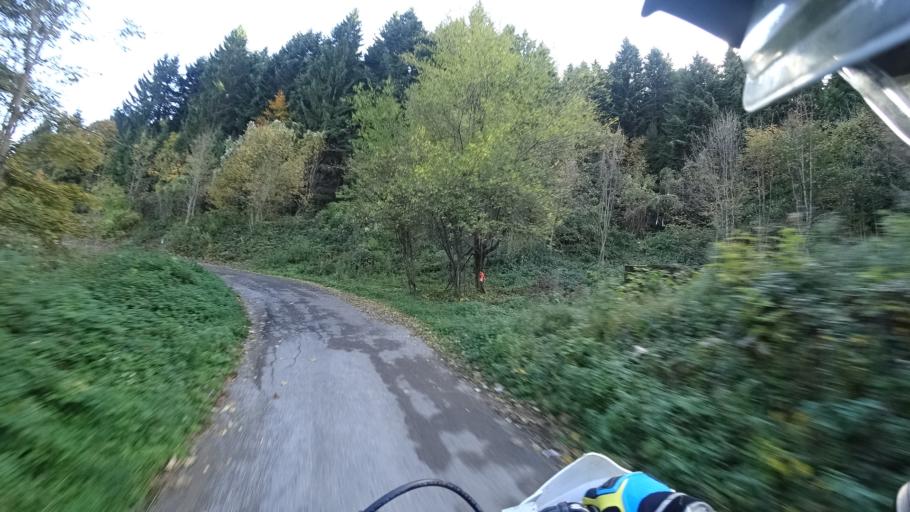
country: HR
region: Karlovacka
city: Plaski
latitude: 44.9799
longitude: 15.4254
